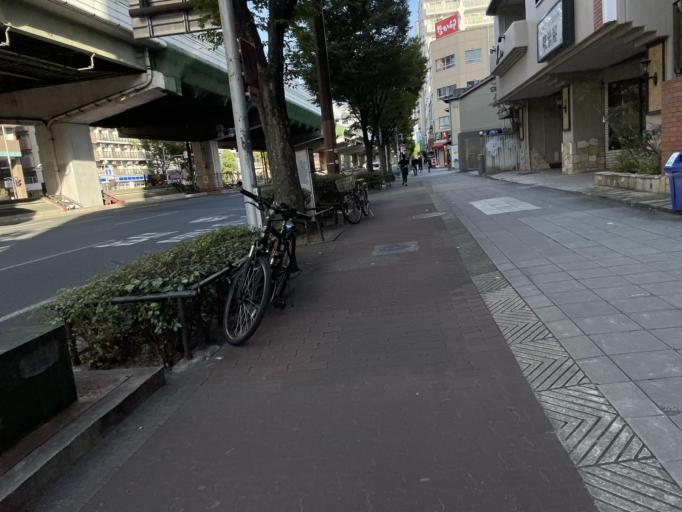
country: JP
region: Osaka
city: Osaka-shi
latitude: 34.6682
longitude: 135.4891
